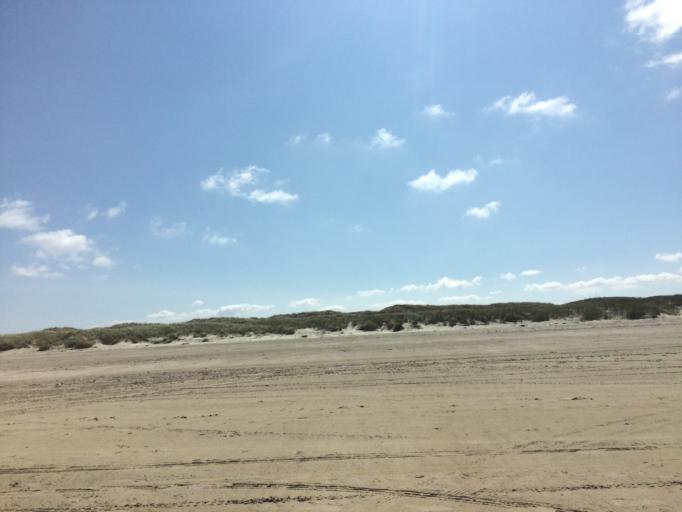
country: DK
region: North Denmark
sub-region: Jammerbugt Kommune
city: Brovst
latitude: 57.2212
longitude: 9.5325
